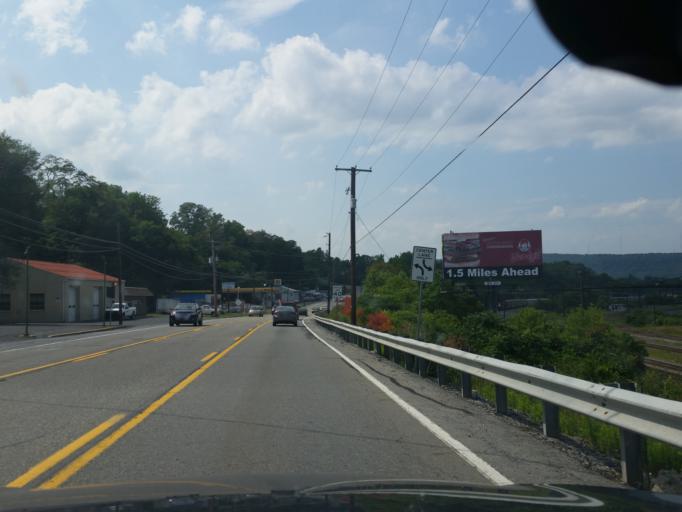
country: US
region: Pennsylvania
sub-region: Cumberland County
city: West Fairview
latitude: 40.2796
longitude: -76.9245
